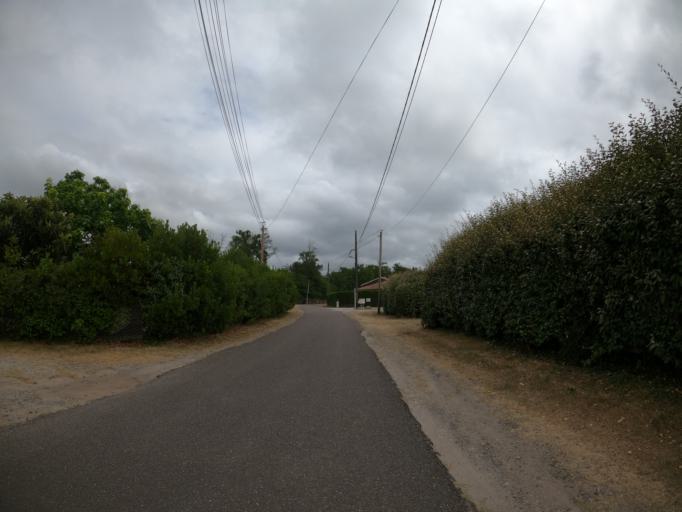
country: FR
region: Aquitaine
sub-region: Departement des Landes
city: Leon
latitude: 43.8850
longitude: -1.3034
